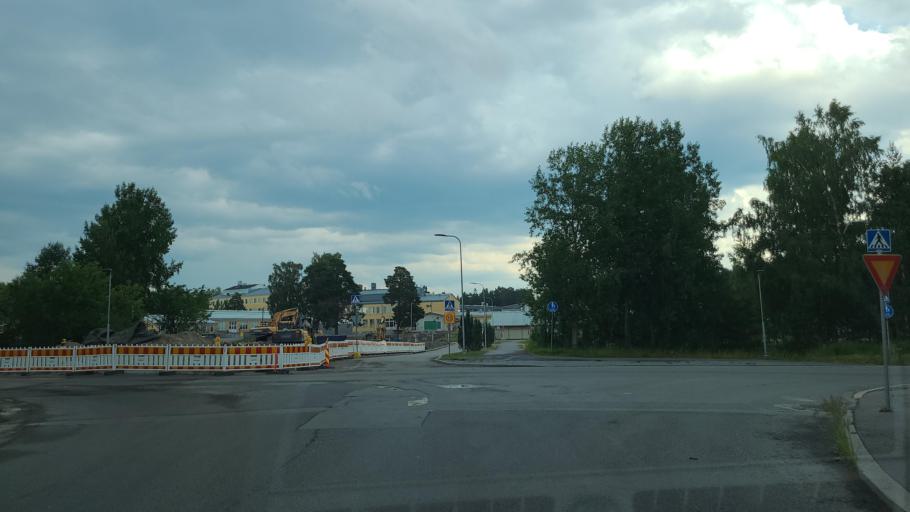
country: FI
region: Ostrobothnia
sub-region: Vaasa
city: Vaasa
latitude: 63.0969
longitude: 21.6384
